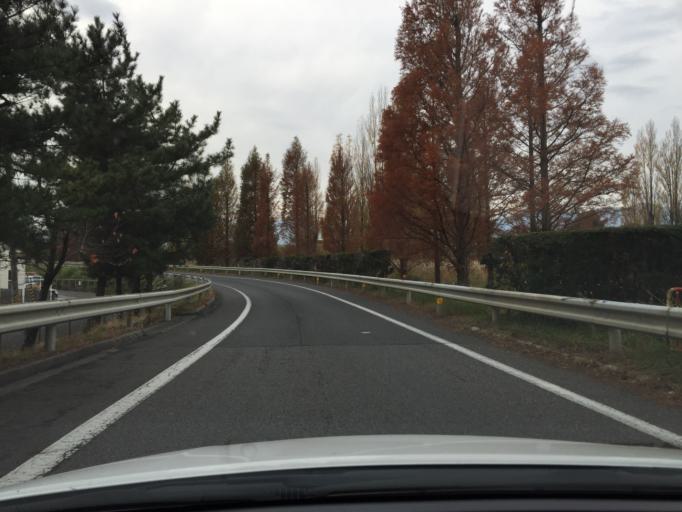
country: JP
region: Fukushima
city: Fukushima-shi
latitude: 37.7374
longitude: 140.4225
